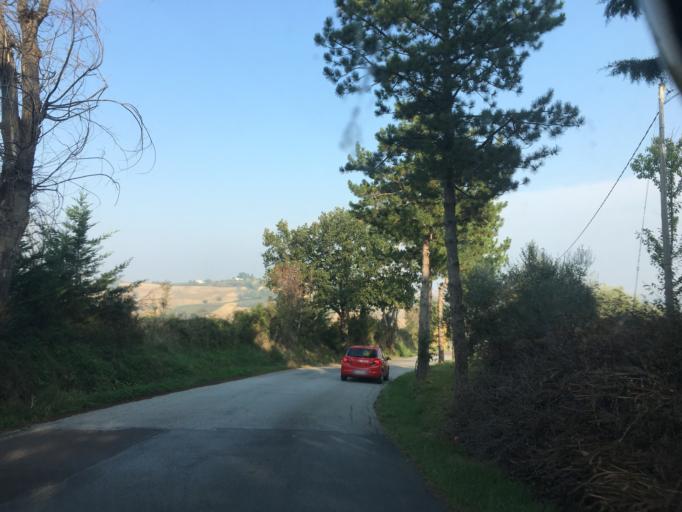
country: IT
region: Emilia-Romagna
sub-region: Provincia di Rimini
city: Coriano
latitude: 43.9501
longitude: 12.6122
